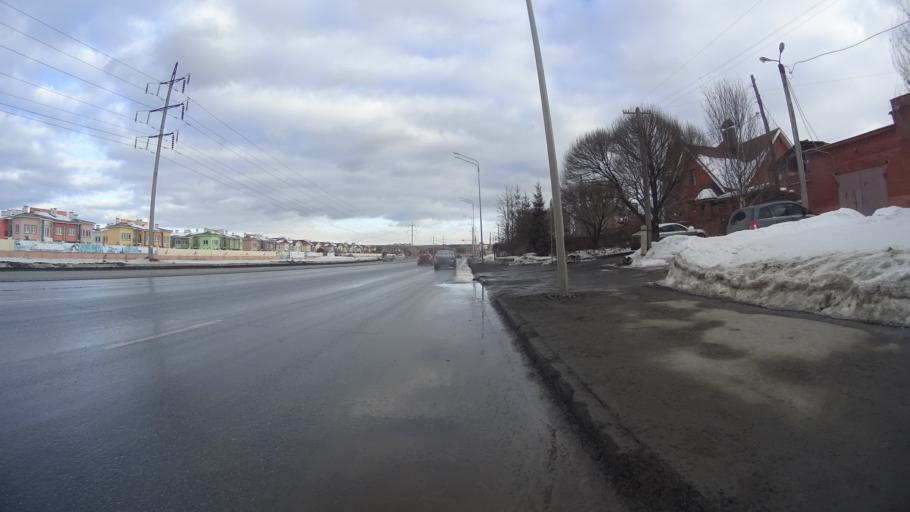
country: RU
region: Chelyabinsk
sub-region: Gorod Chelyabinsk
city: Chelyabinsk
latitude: 55.1558
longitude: 61.3104
